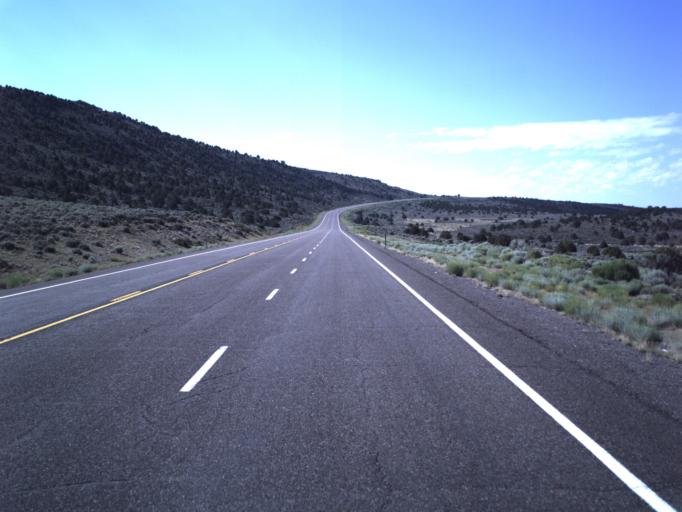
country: US
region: Utah
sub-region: Wayne County
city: Loa
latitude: 38.4928
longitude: -111.8325
